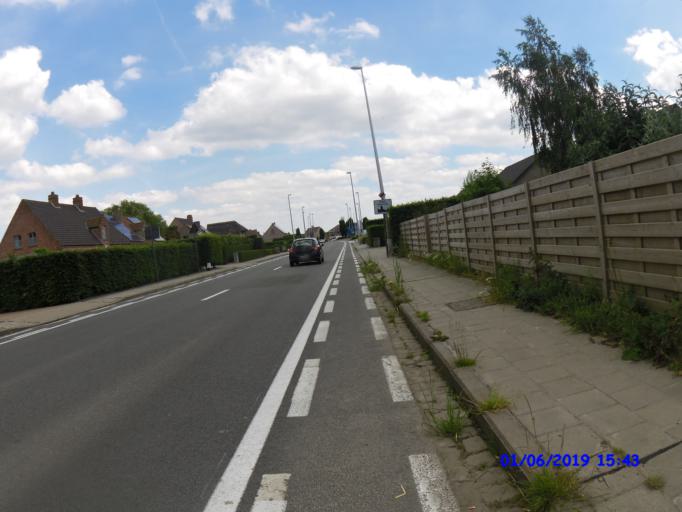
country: BE
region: Flanders
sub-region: Provincie West-Vlaanderen
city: Diksmuide
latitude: 51.0284
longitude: 2.8878
